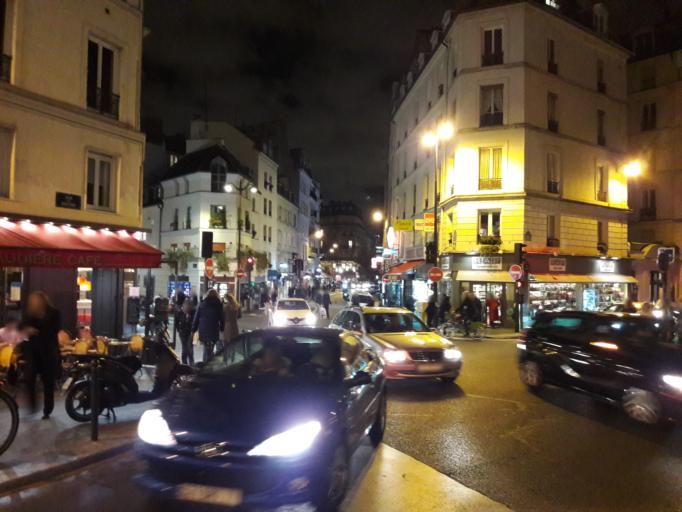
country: FR
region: Ile-de-France
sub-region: Paris
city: Saint-Ouen
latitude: 48.8768
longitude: 2.3392
